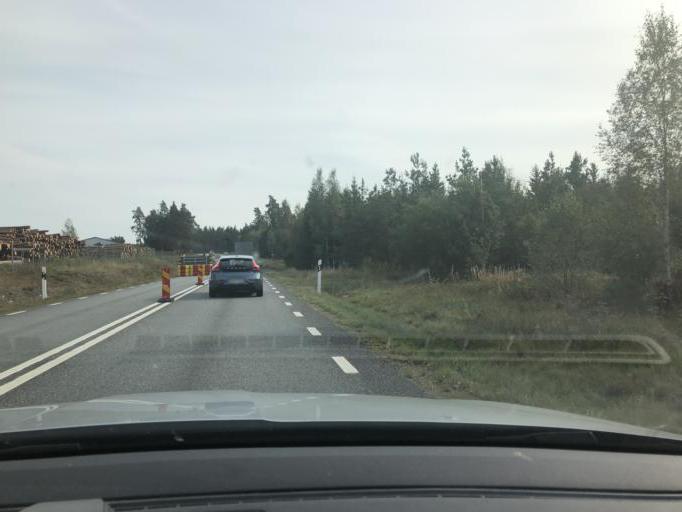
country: SE
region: Joenkoeping
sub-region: Vetlanda Kommun
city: Ekenassjon
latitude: 57.5561
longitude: 14.9818
